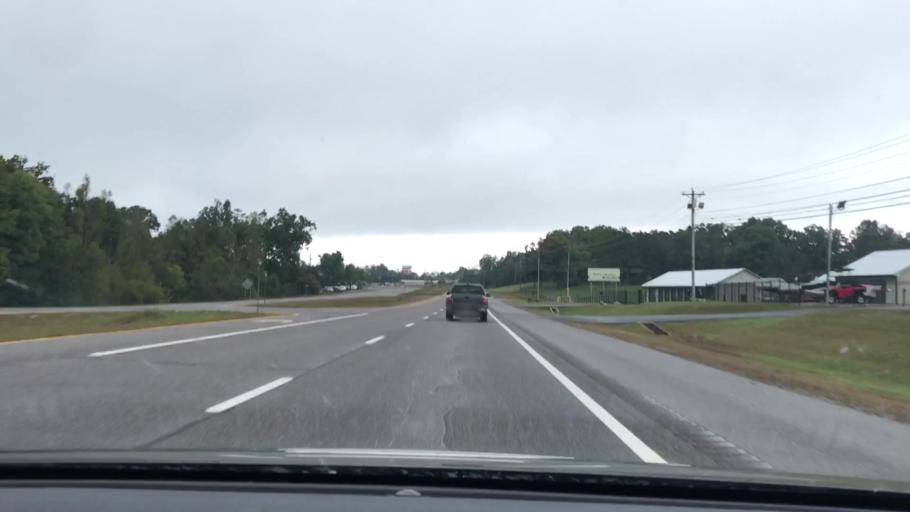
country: US
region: Tennessee
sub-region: Fentress County
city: Jamestown
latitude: 36.3827
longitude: -84.9407
